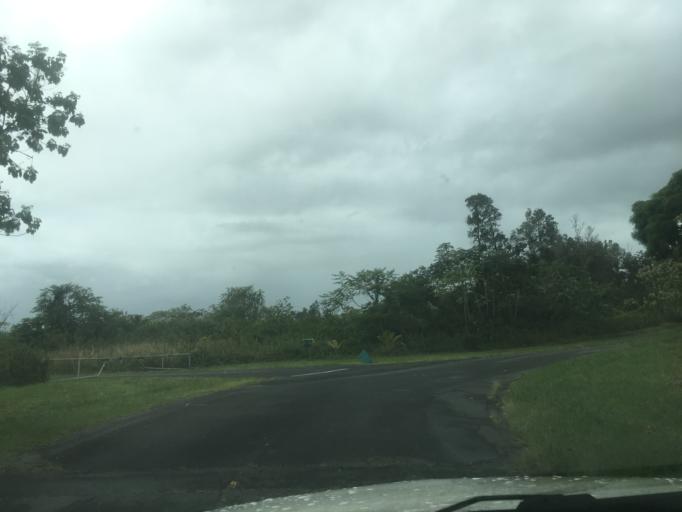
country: US
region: Hawaii
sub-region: Hawaii County
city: Leilani Estates
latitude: 19.4686
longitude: -154.8665
